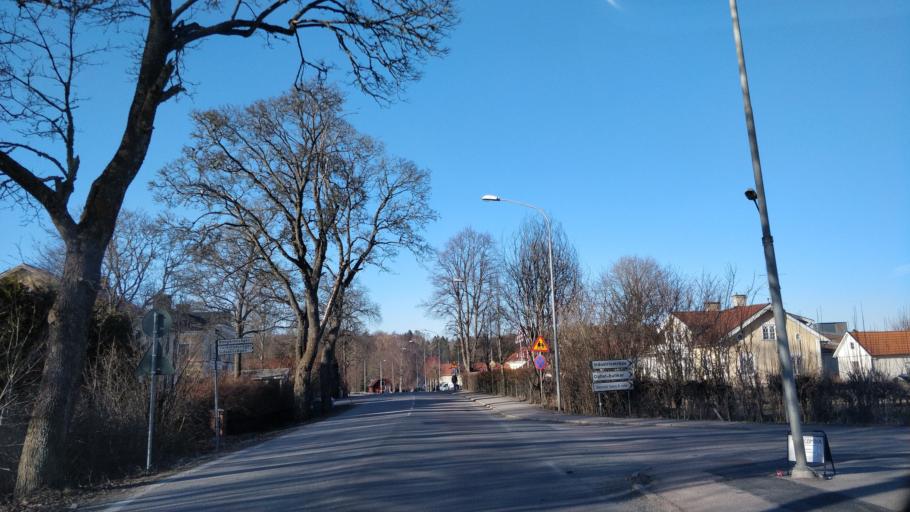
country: SE
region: Uppsala
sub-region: Enkopings Kommun
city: Orsundsbro
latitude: 59.7346
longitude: 17.3087
